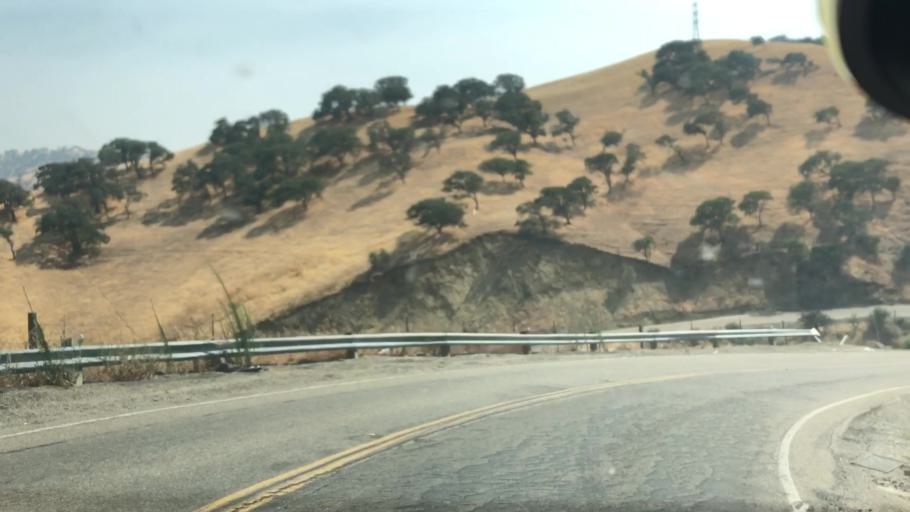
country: US
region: California
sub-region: San Joaquin County
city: Mountain House
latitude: 37.6495
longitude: -121.6005
